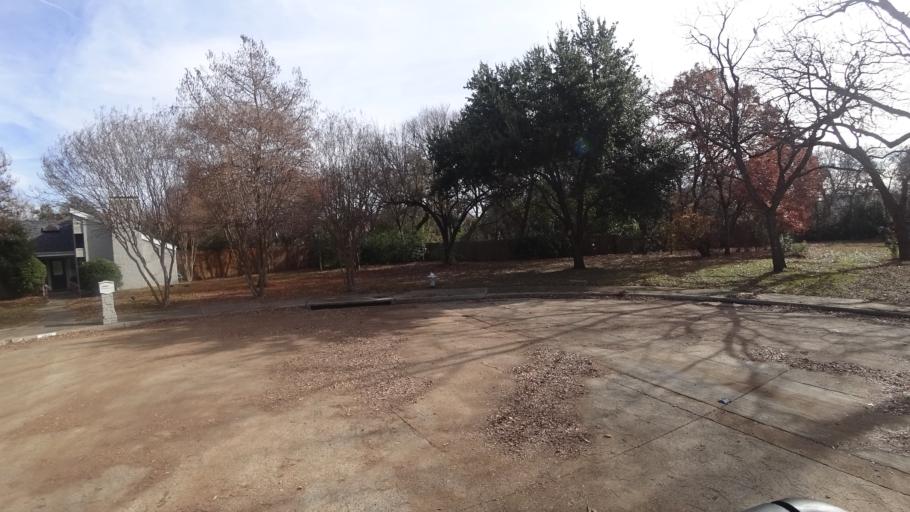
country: US
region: Texas
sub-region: Denton County
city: Highland Village
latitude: 33.0802
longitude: -97.0434
